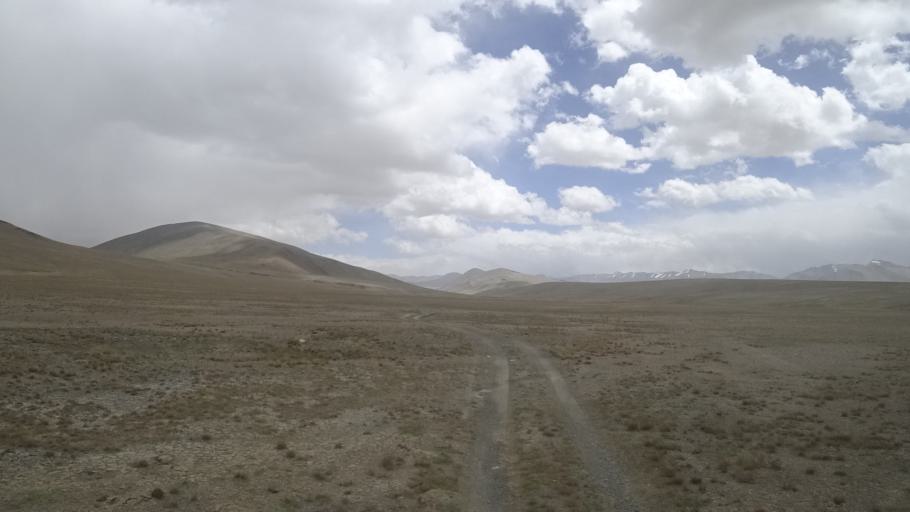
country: TJ
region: Gorno-Badakhshan
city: Murghob
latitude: 37.4903
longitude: 74.0241
